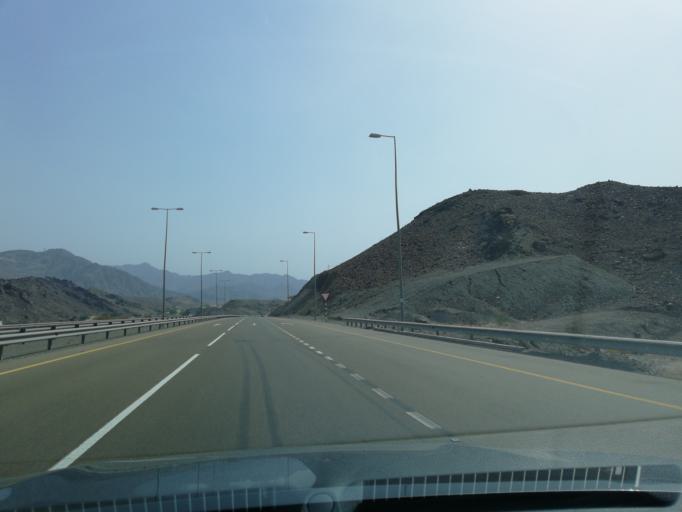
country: OM
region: Al Batinah
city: Al Liwa'
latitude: 24.2323
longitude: 56.3393
